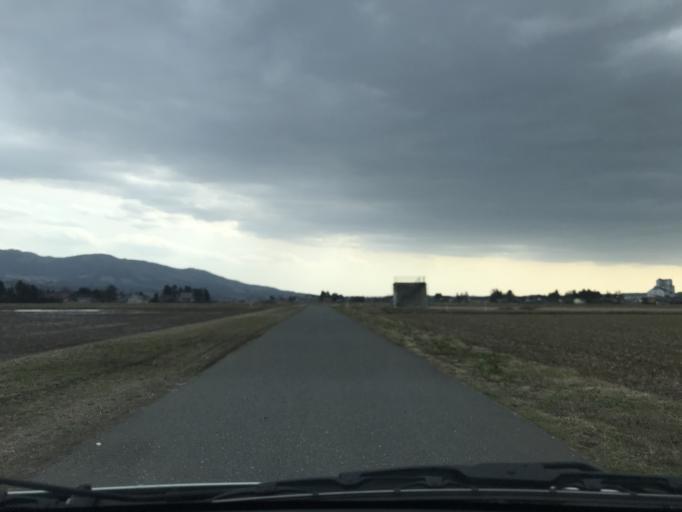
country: JP
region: Iwate
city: Mizusawa
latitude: 39.0750
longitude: 141.1555
